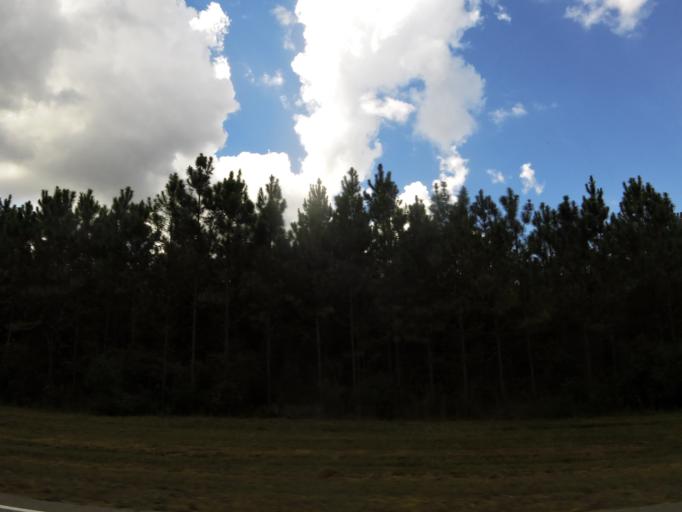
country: US
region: Georgia
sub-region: Charlton County
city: Folkston
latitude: 30.9663
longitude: -82.0242
